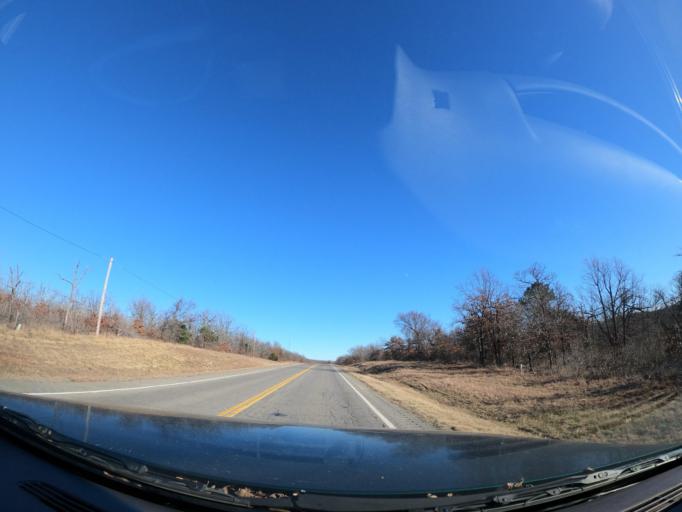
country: US
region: Oklahoma
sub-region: Pittsburg County
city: Longtown
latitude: 35.2253
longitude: -95.4416
